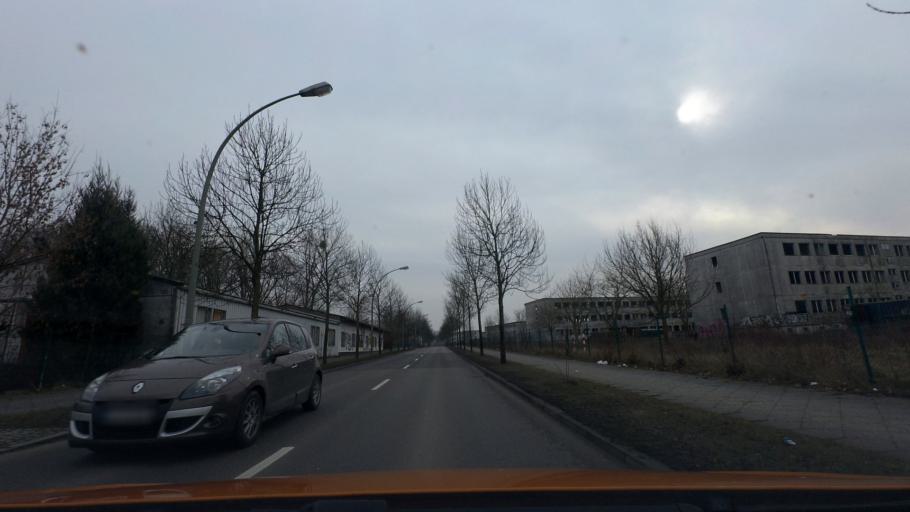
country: DE
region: Berlin
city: Blankenburg
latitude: 52.5874
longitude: 13.4569
